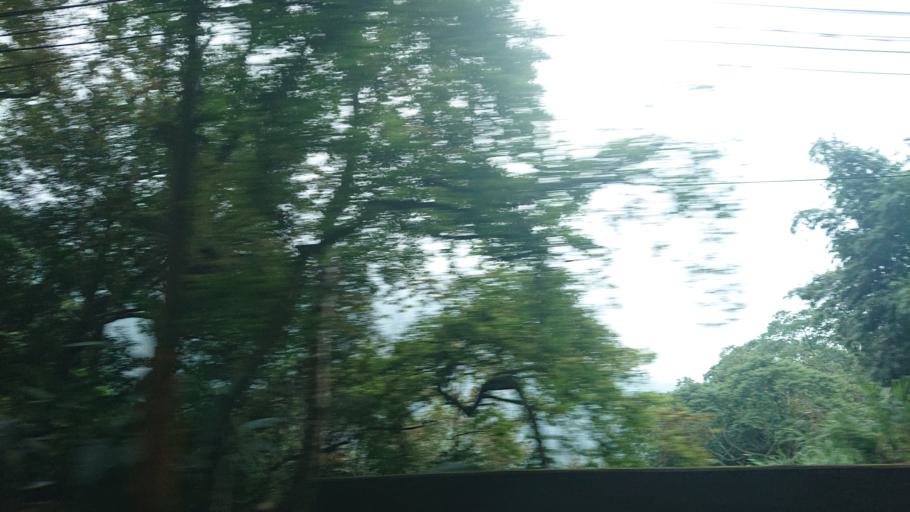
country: TW
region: Taiwan
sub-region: Chiayi
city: Jiayi Shi
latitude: 23.4741
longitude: 120.7110
